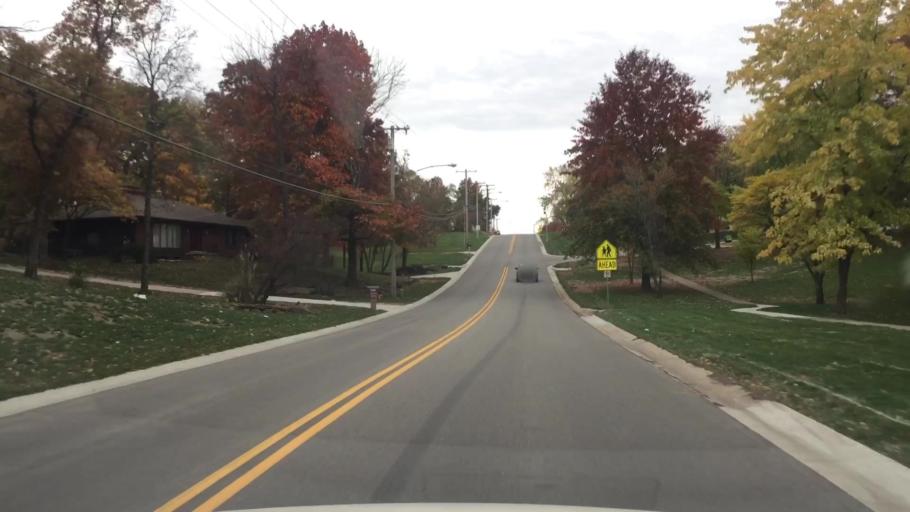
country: US
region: Kansas
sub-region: Johnson County
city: Shawnee
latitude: 39.0411
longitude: -94.7240
